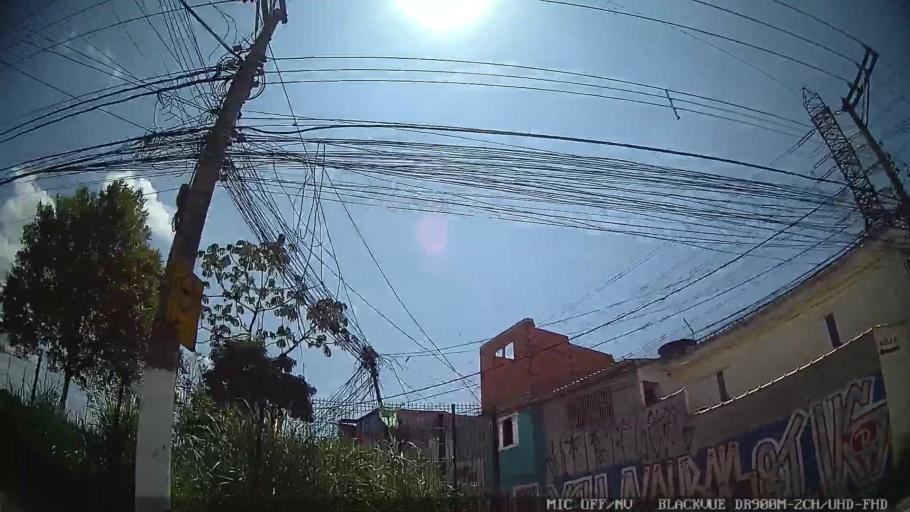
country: BR
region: Sao Paulo
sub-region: Guarulhos
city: Guarulhos
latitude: -23.5171
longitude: -46.4857
